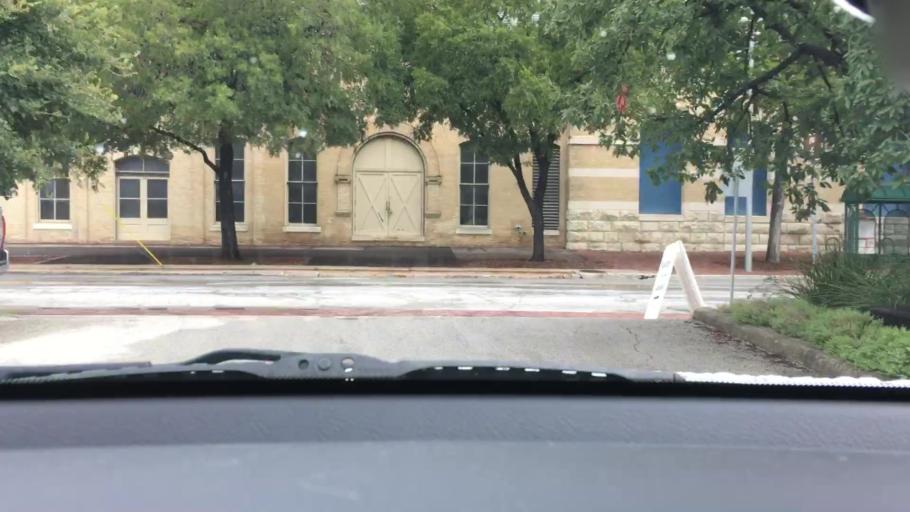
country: US
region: Texas
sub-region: Bexar County
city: San Antonio
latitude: 29.4373
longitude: -98.4828
